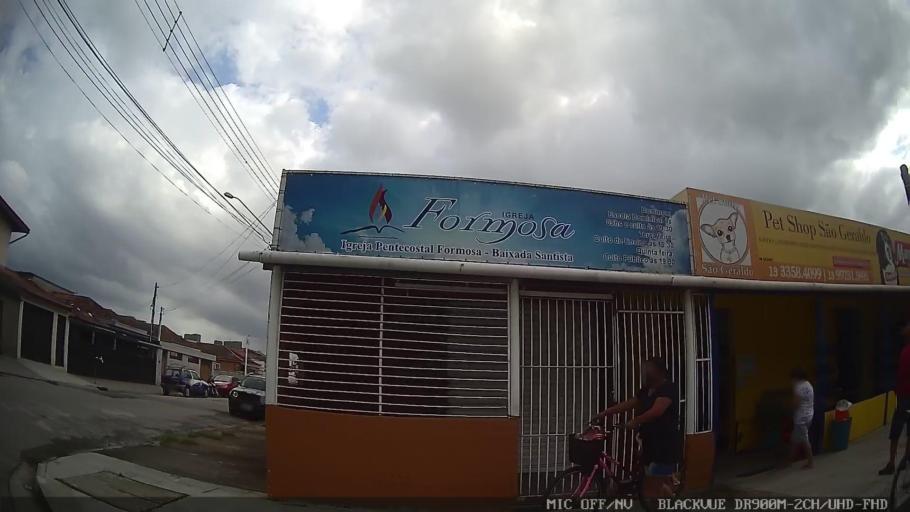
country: BR
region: Sao Paulo
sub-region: Guaruja
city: Guaruja
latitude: -23.9933
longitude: -46.2874
